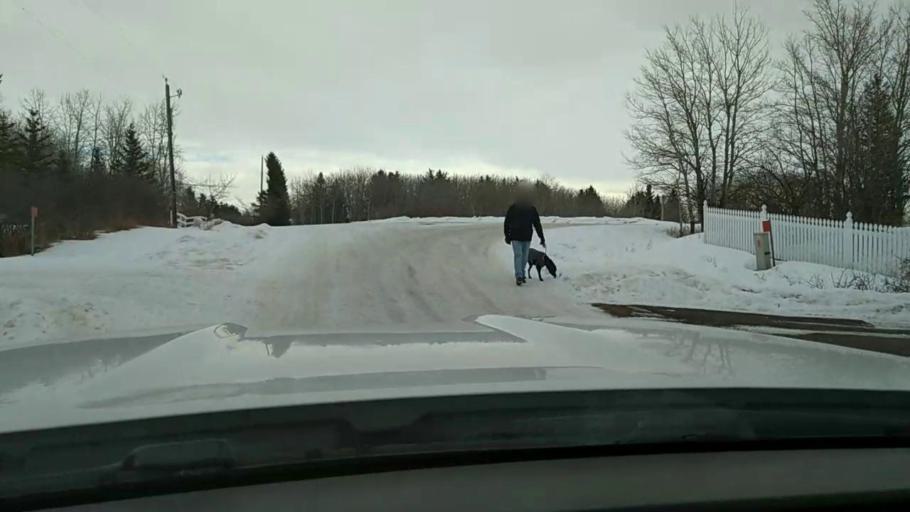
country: CA
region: Alberta
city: Cochrane
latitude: 51.1976
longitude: -114.2769
